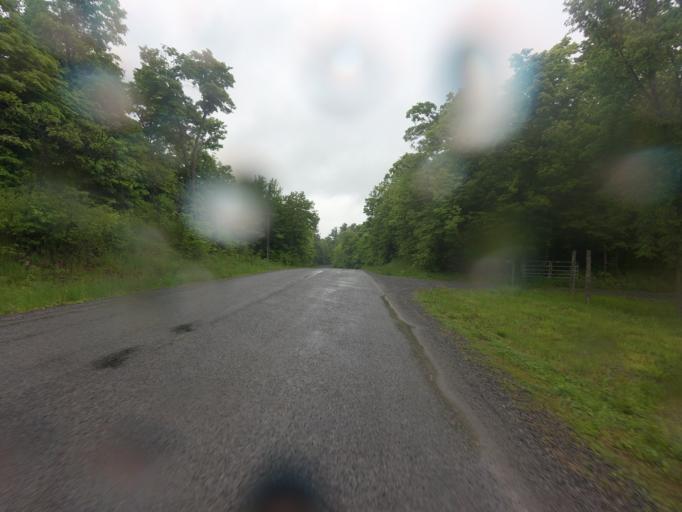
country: CA
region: Ontario
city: Gananoque
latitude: 44.5429
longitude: -76.3702
